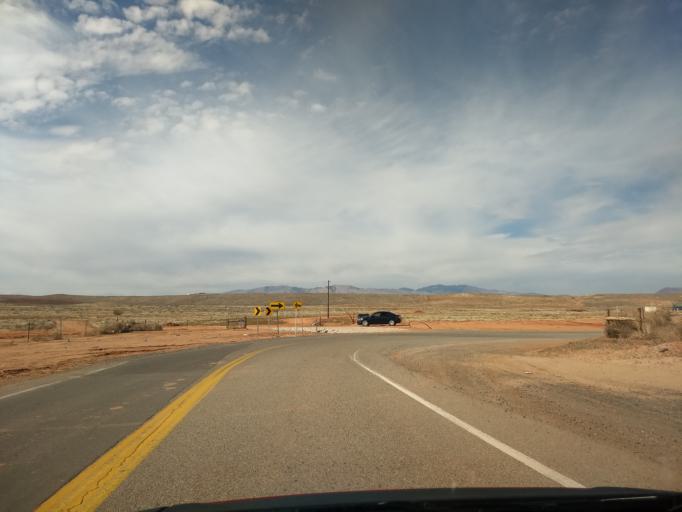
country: US
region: Utah
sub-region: Washington County
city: Washington
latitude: 37.0592
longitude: -113.4898
